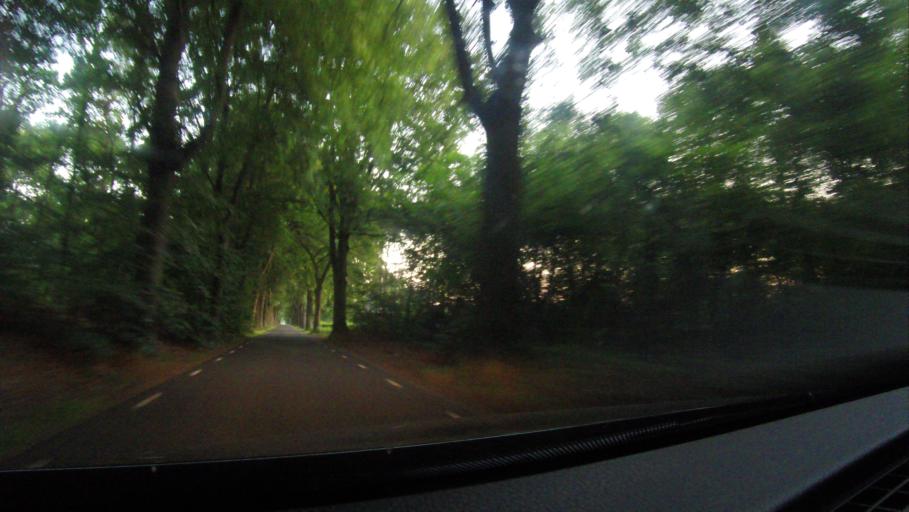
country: NL
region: Gelderland
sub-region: Gemeente Lochem
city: Harfsen
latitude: 52.2616
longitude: 6.2815
